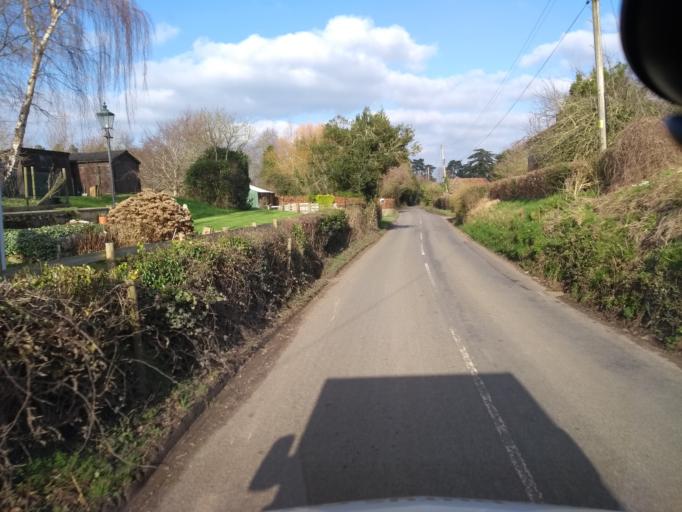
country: GB
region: England
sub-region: Somerset
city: Creech Saint Michael
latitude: 50.9773
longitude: -3.0559
